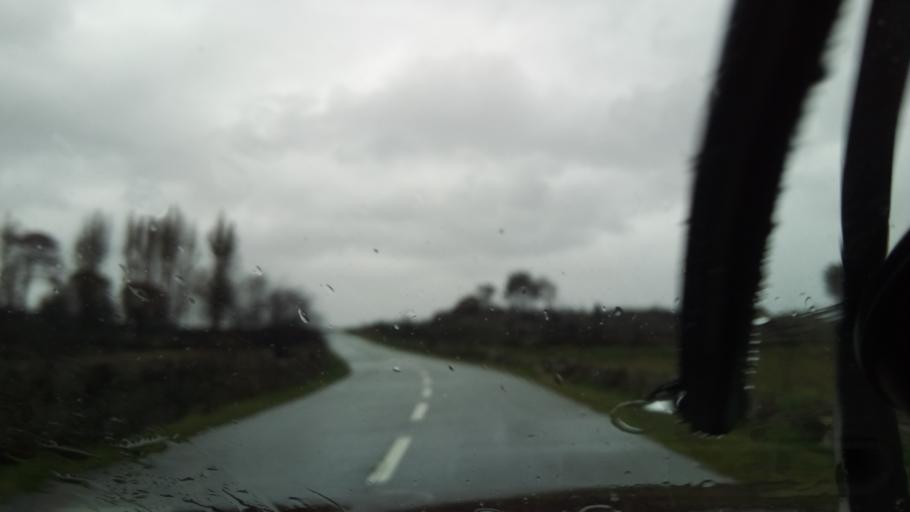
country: PT
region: Guarda
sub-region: Fornos de Algodres
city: Fornos de Algodres
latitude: 40.5591
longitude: -7.5189
